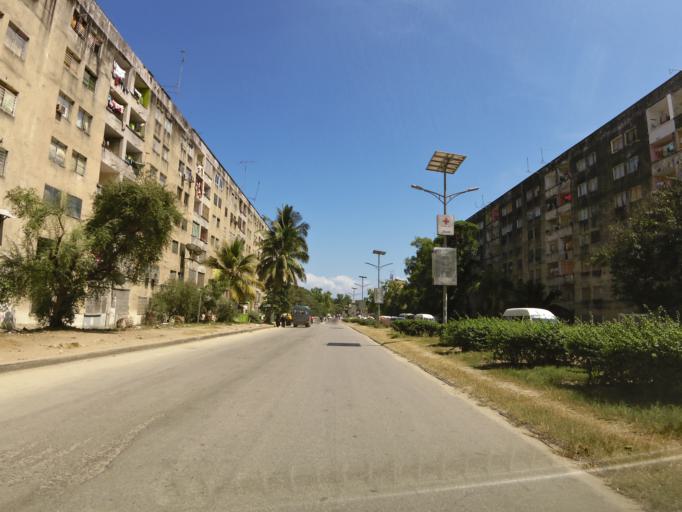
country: TZ
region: Zanzibar Urban/West
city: Zanzibar
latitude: -6.1650
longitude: 39.1970
